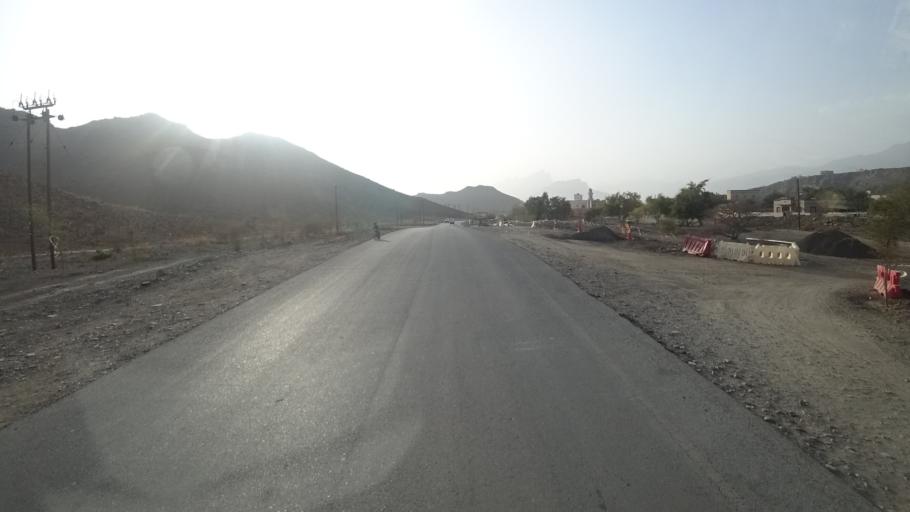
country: OM
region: Muhafazat ad Dakhiliyah
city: Bahla'
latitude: 23.0799
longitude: 57.3330
